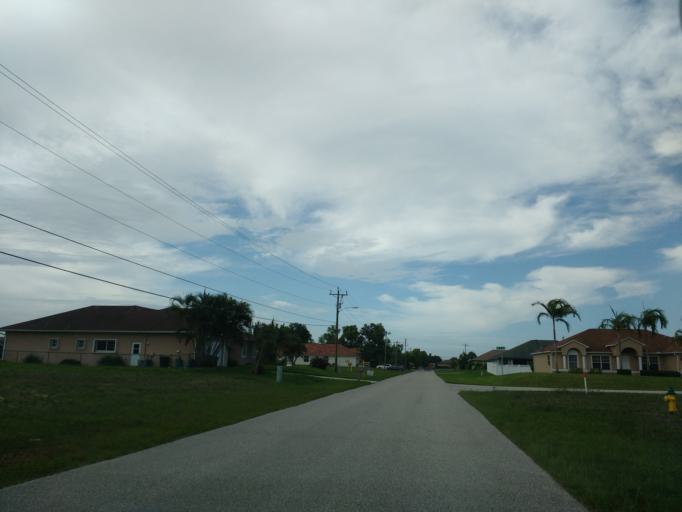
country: US
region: Florida
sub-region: Lee County
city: Cape Coral
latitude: 26.5949
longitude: -82.0235
